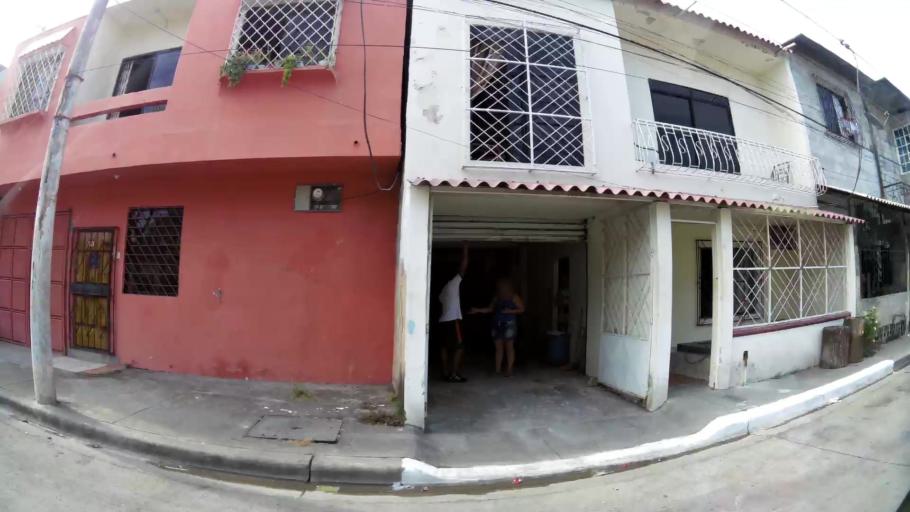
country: EC
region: Guayas
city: Guayaquil
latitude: -2.2583
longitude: -79.8765
